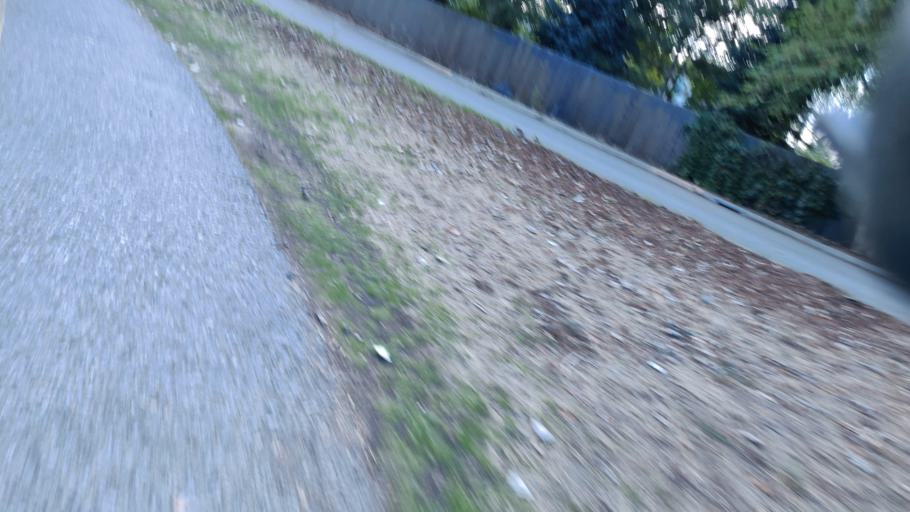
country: US
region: Idaho
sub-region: Ada County
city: Boise
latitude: 43.6014
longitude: -116.1764
